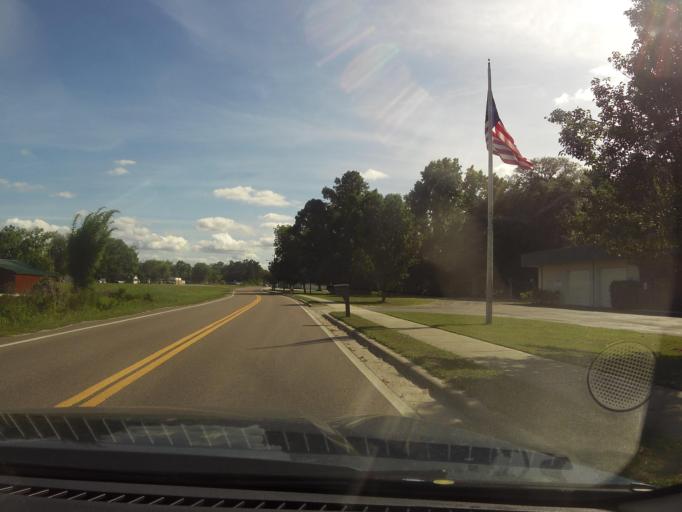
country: US
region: Florida
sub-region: Nassau County
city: Callahan
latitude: 30.5648
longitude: -81.8333
